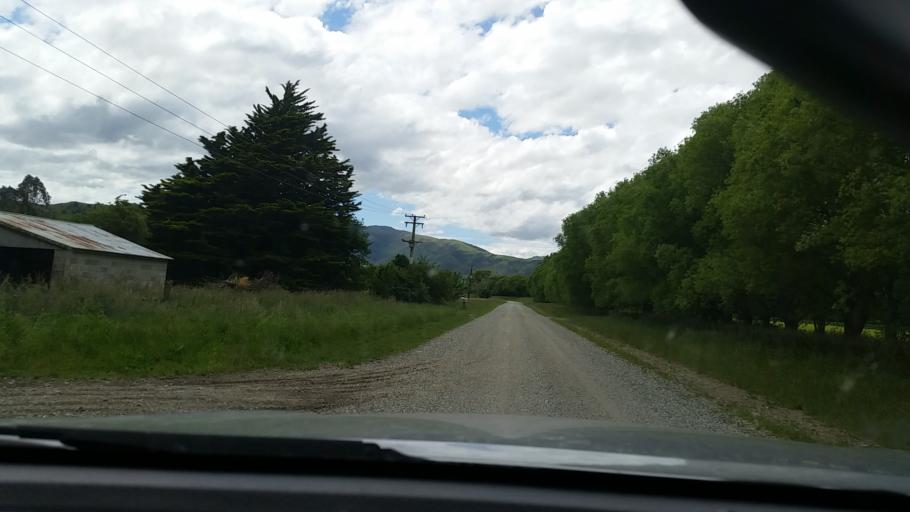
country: NZ
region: Otago
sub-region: Queenstown-Lakes District
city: Kingston
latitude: -45.7324
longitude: 168.6641
